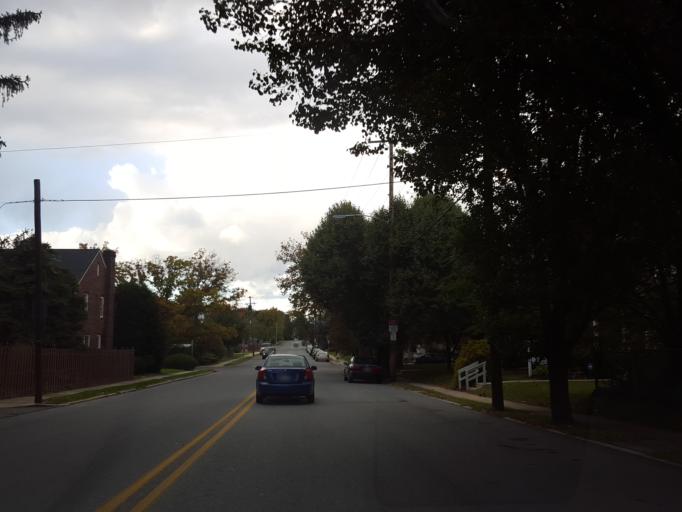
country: US
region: Pennsylvania
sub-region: York County
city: Valley View
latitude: 39.9493
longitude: -76.7131
